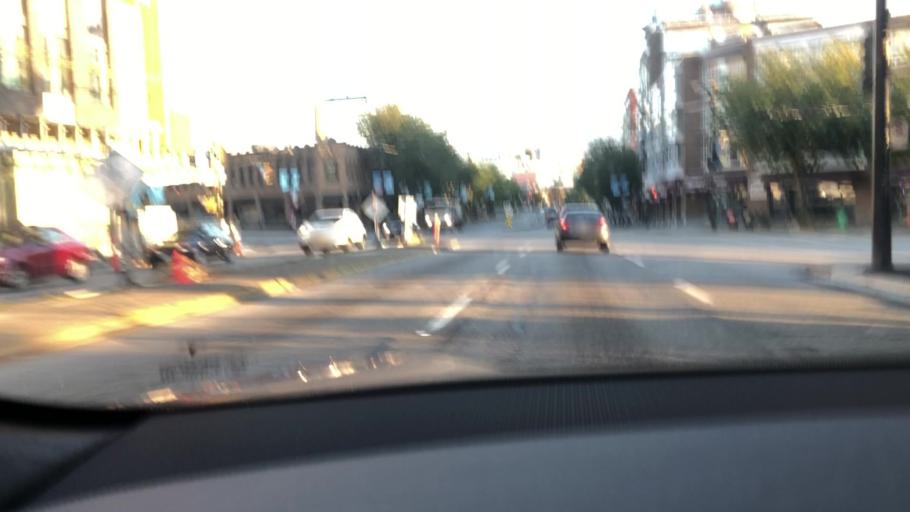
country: CA
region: British Columbia
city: Vancouver
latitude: 49.2624
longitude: -123.0990
